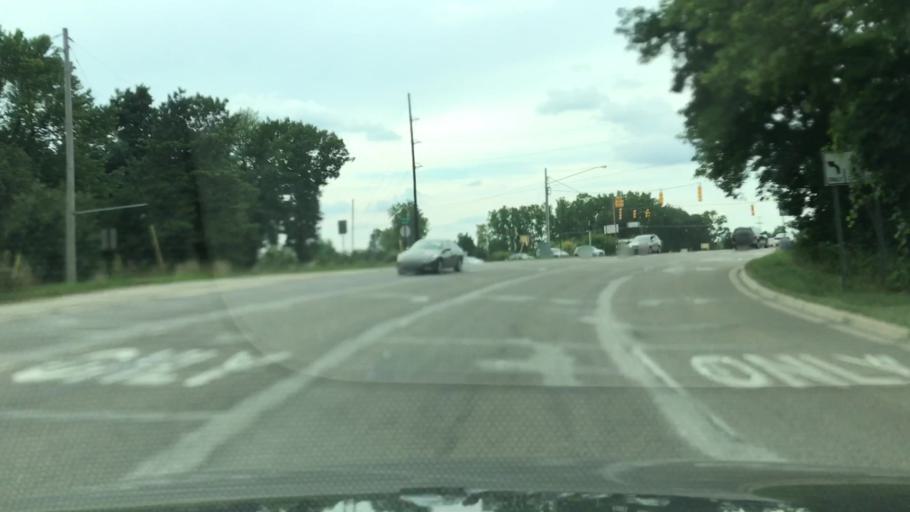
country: US
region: Michigan
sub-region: Kent County
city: East Grand Rapids
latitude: 42.9619
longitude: -85.5577
